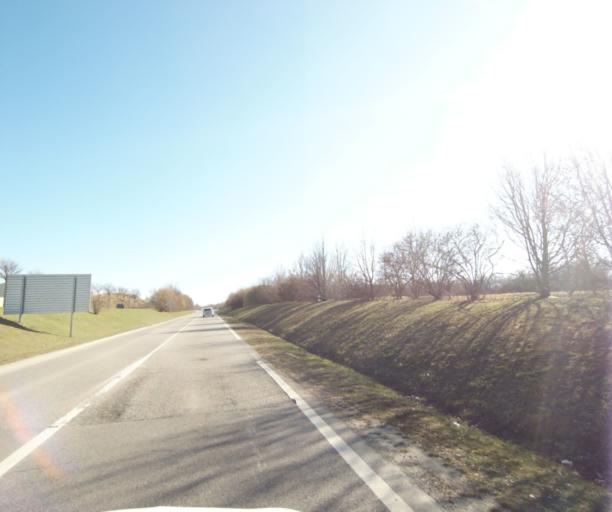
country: FR
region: Lorraine
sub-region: Departement de Meurthe-et-Moselle
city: Tomblaine
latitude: 48.6828
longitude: 6.2222
